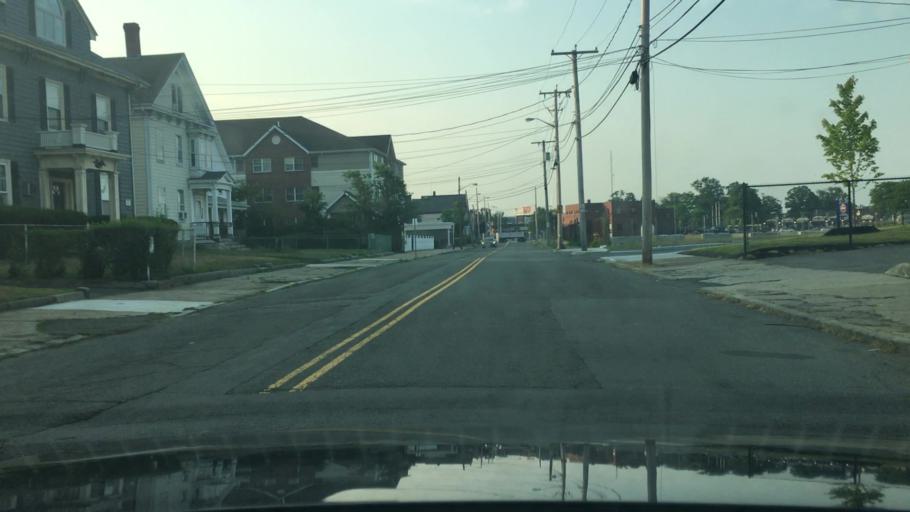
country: US
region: Massachusetts
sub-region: Essex County
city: Lynn
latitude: 42.4655
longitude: -70.9665
